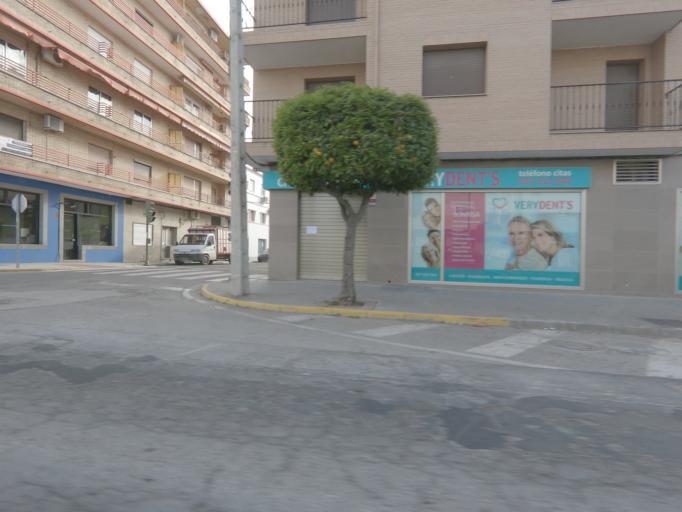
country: ES
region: Extremadura
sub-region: Provincia de Caceres
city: Moraleja
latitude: 40.0693
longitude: -6.6567
